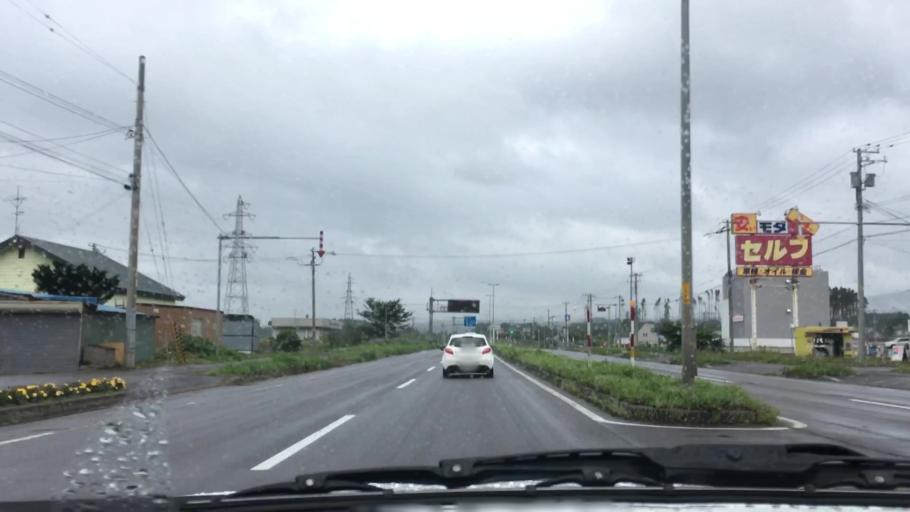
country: JP
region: Hokkaido
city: Nanae
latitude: 42.2479
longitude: 140.2879
